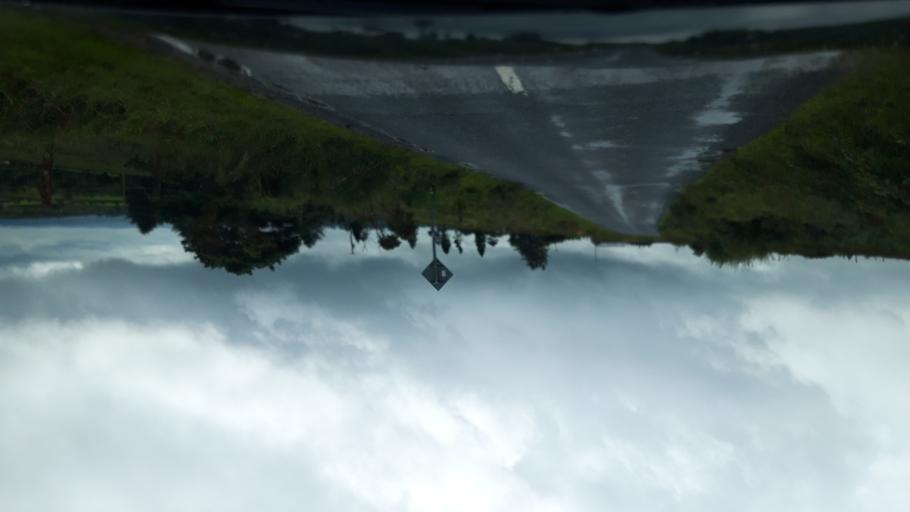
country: IE
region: Munster
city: Cahir
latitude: 52.1976
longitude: -7.9026
